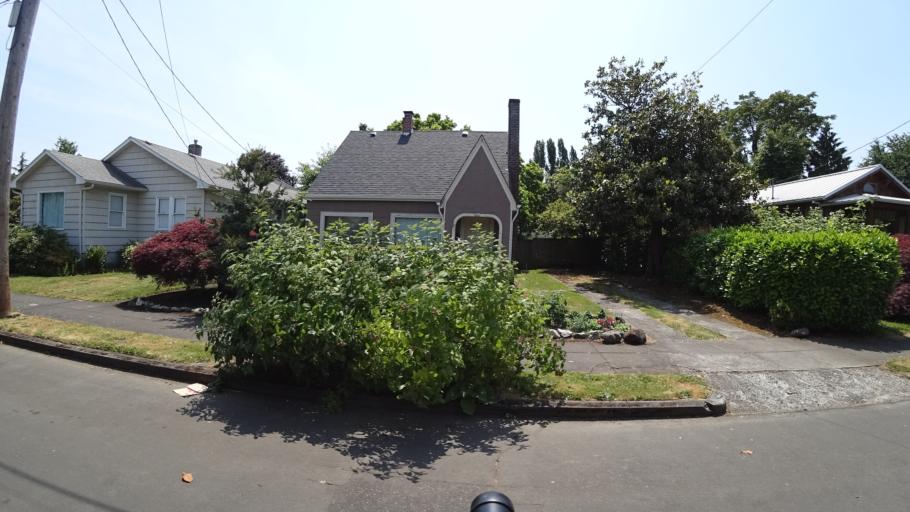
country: US
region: Oregon
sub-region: Multnomah County
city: Portland
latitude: 45.5800
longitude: -122.6749
